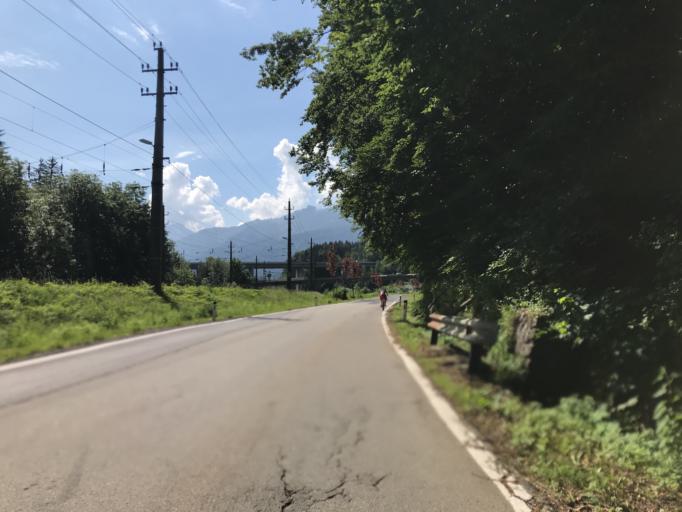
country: AT
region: Carinthia
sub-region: Politischer Bezirk Villach Land
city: Finkenstein am Faaker See
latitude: 46.5786
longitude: 13.8328
